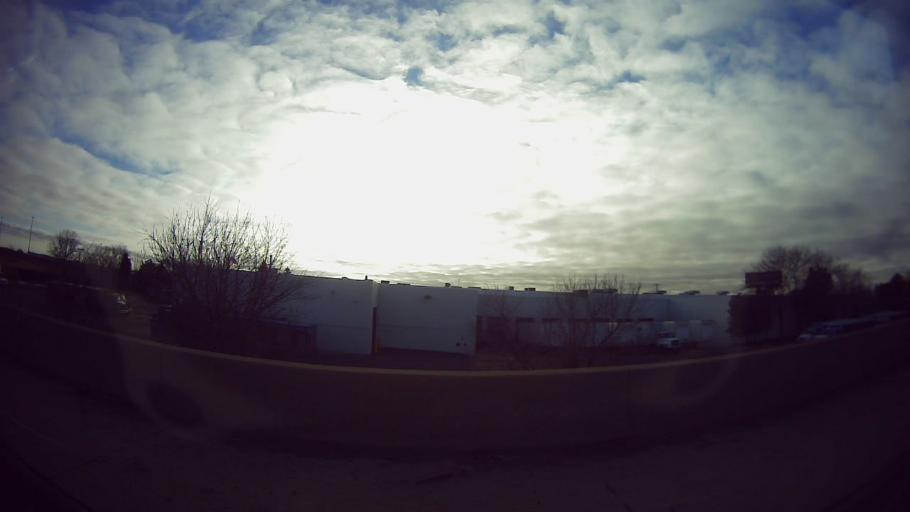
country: US
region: Michigan
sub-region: Wayne County
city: Highland Park
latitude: 42.4116
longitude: -83.0823
